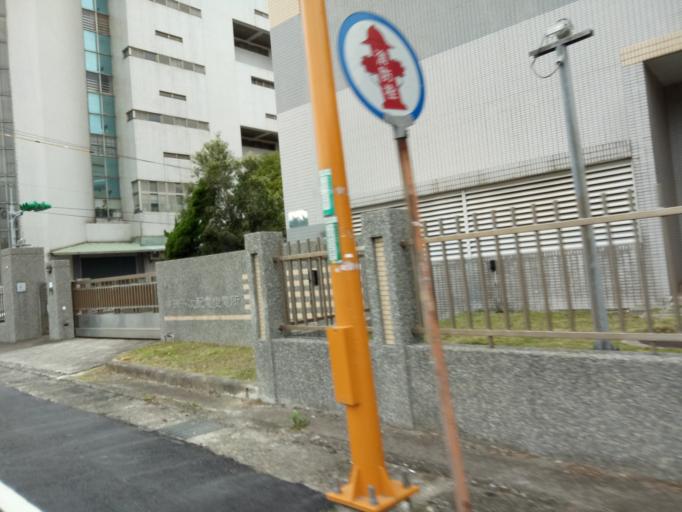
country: TW
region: Taiwan
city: Daxi
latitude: 24.8689
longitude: 121.2573
